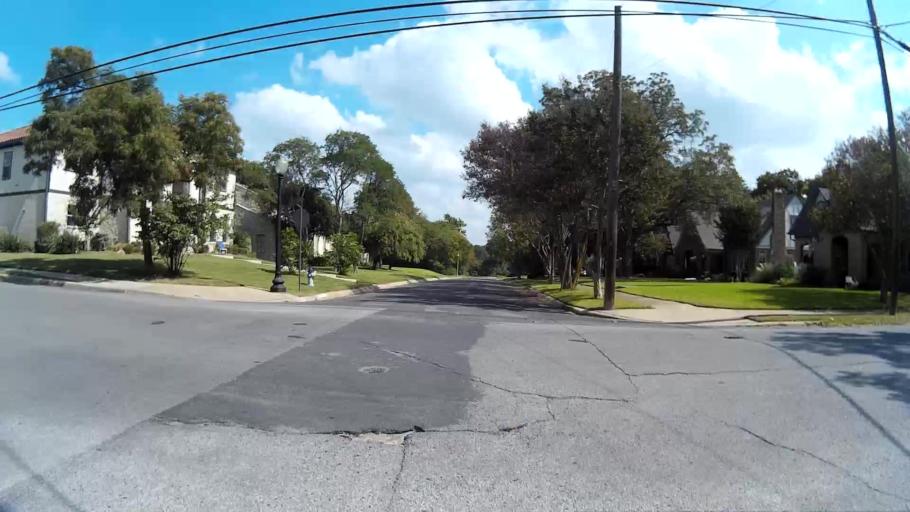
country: US
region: Texas
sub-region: Dallas County
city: Highland Park
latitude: 32.8095
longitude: -96.7519
